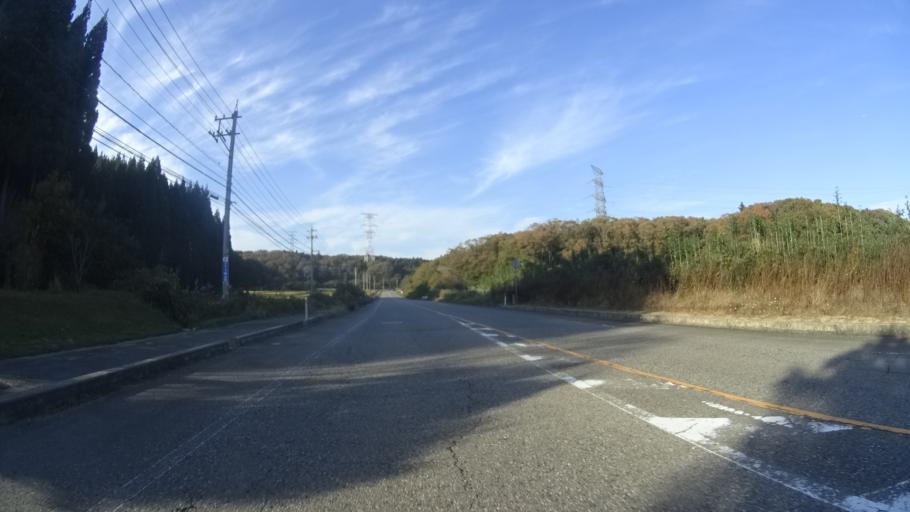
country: JP
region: Ishikawa
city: Hakui
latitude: 37.0445
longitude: 136.7758
